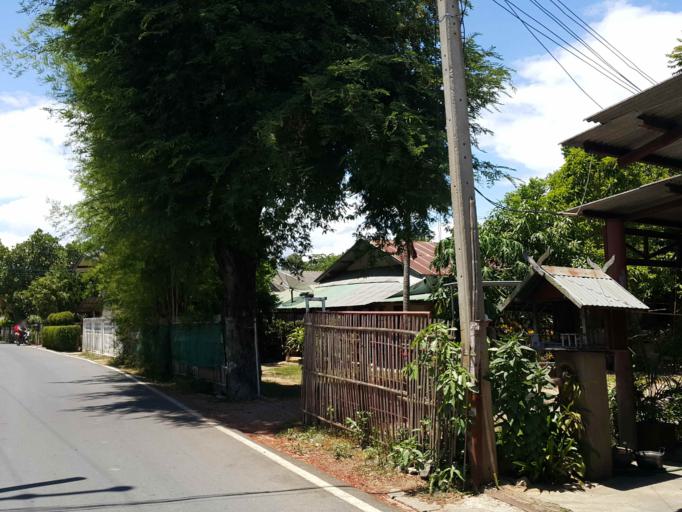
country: TH
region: Chiang Mai
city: Saraphi
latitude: 18.7480
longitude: 99.0135
